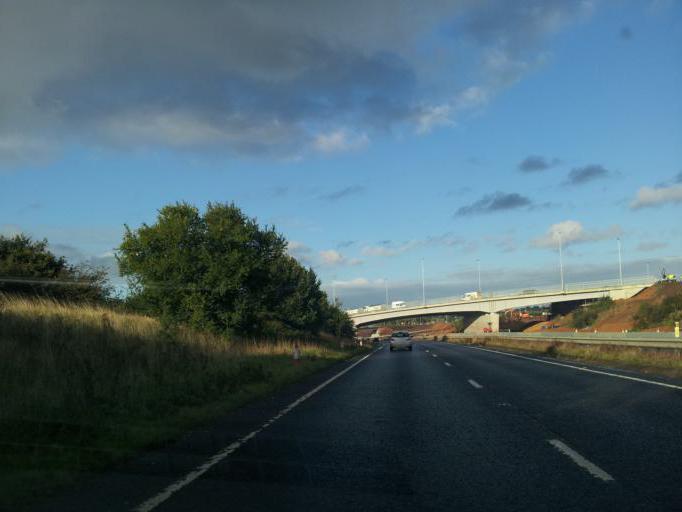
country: GB
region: England
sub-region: Norfolk
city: Surlingham
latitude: 52.6261
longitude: 1.3852
